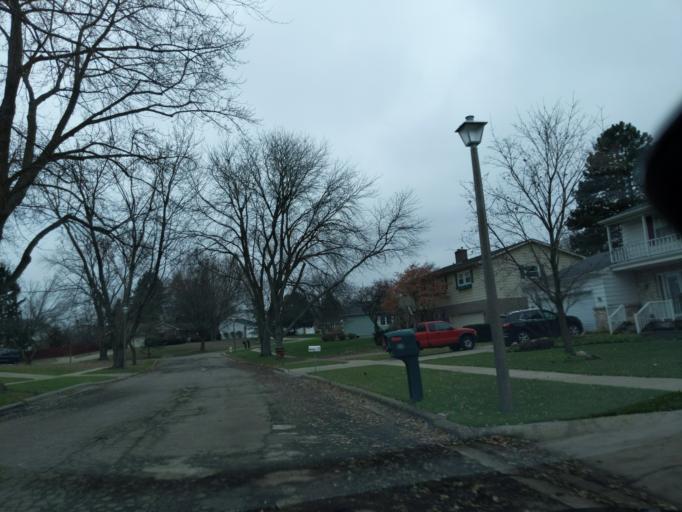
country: US
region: Michigan
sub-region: Eaton County
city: Waverly
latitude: 42.7239
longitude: -84.6283
